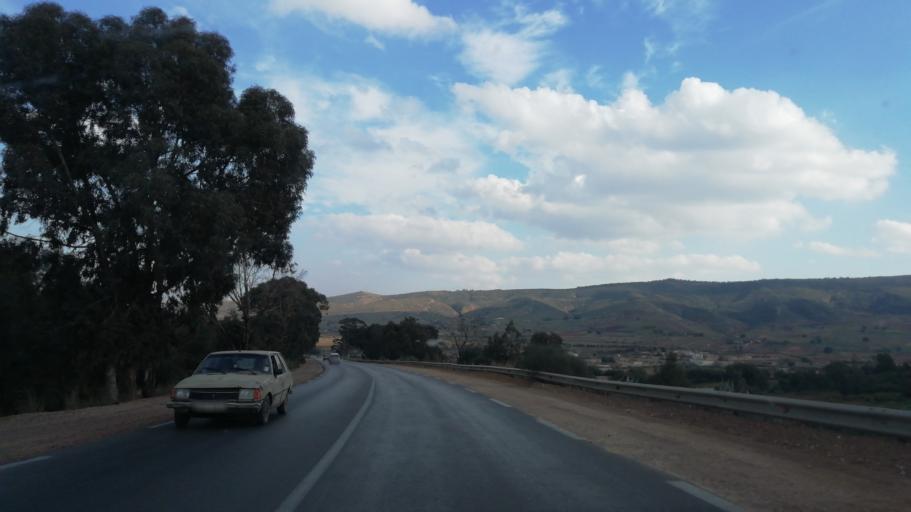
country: DZ
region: Relizane
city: Relizane
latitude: 35.9027
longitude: 0.4441
